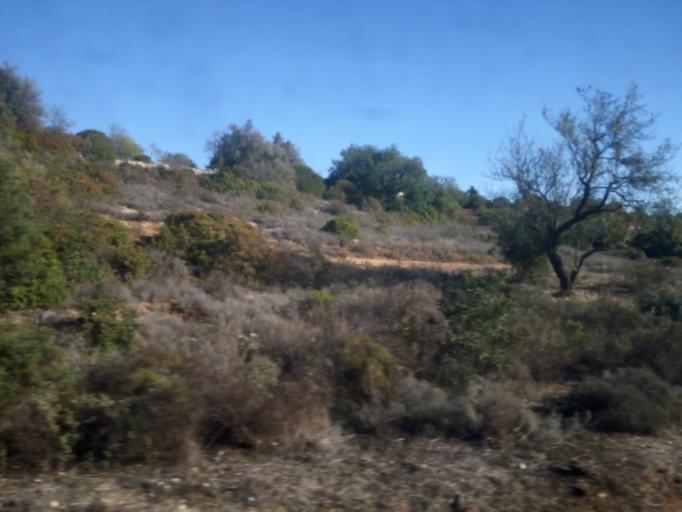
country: PT
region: Faro
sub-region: Albufeira
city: Ferreiras
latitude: 37.1473
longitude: -8.2491
